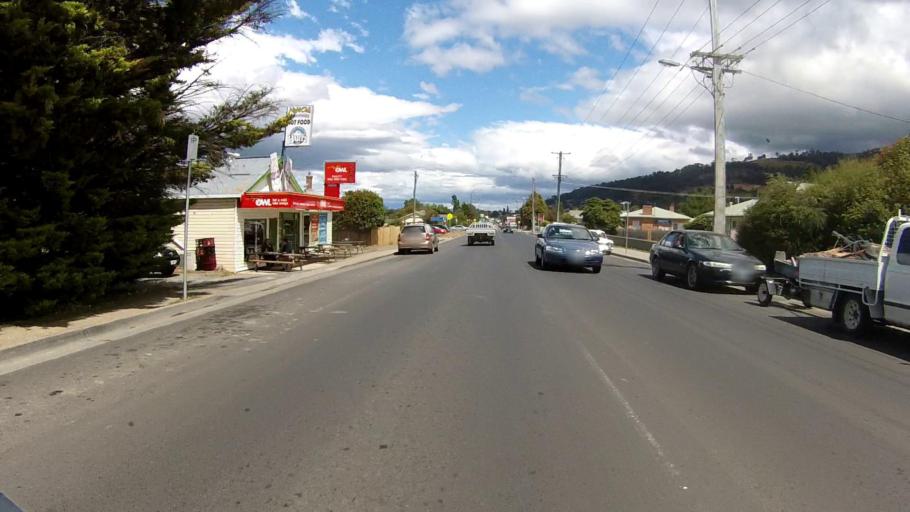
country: AU
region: Tasmania
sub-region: Huon Valley
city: Huonville
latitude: -43.0259
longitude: 147.0511
